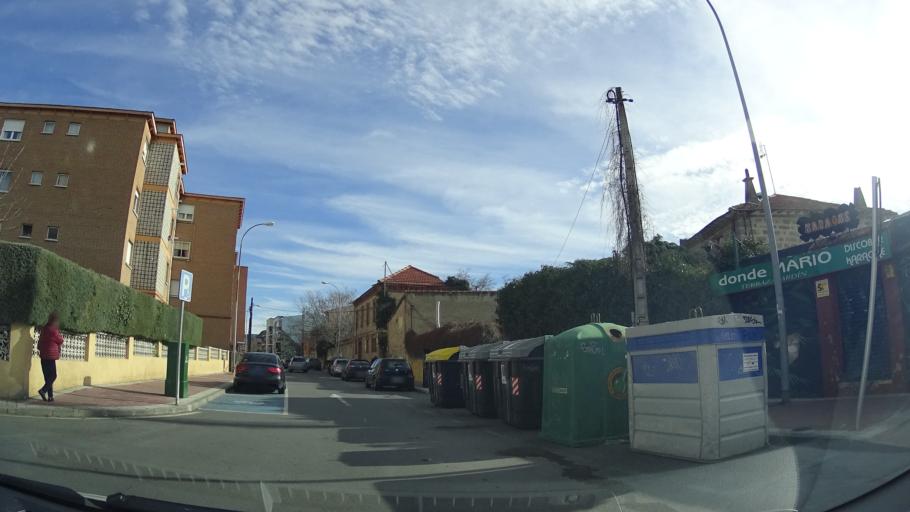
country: ES
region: Madrid
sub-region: Provincia de Madrid
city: Collado-Villalba
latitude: 40.6274
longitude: -4.0133
